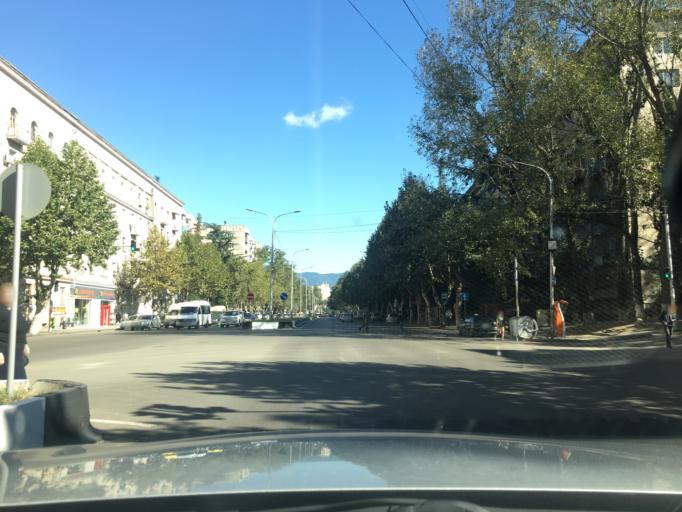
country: GE
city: Zahesi
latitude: 41.7624
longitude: 44.7885
